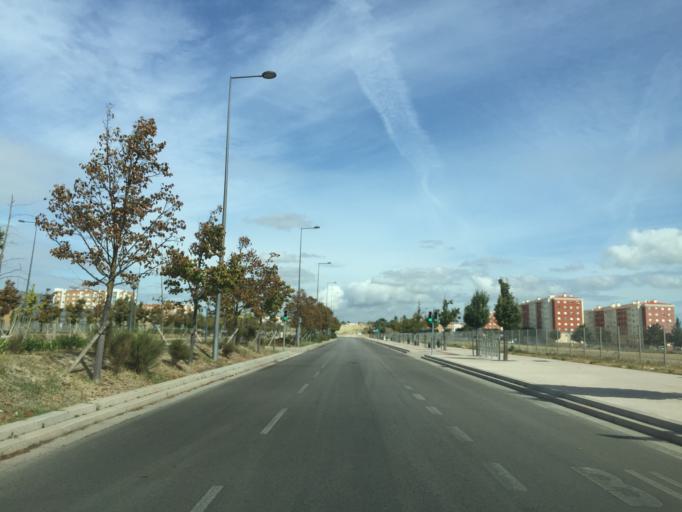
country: PT
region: Lisbon
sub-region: Odivelas
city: Olival do Basto
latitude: 38.7748
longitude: -9.1481
